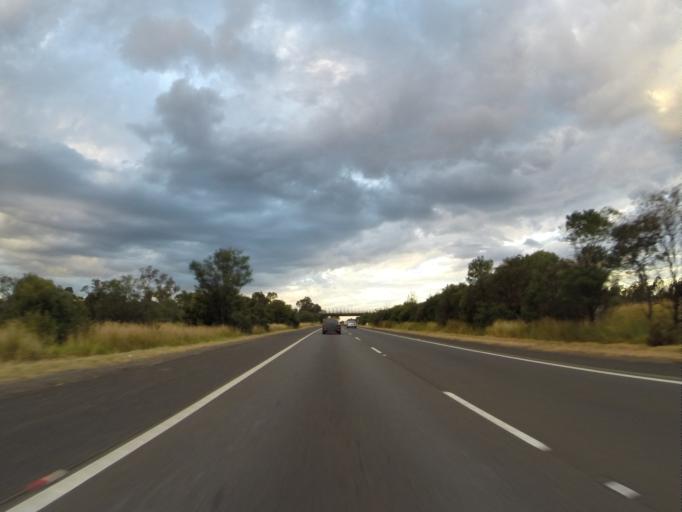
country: AU
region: New South Wales
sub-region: Wollondilly
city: Douglas Park
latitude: -34.1845
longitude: 150.7191
